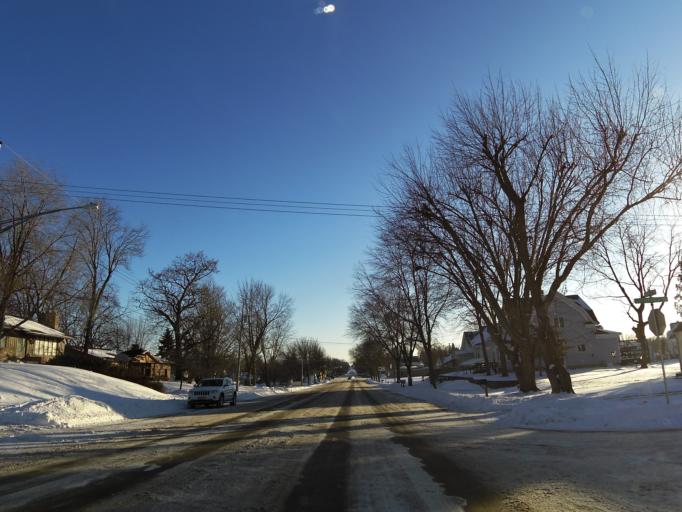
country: US
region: Minnesota
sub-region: Rice County
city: Lonsdale
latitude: 44.4837
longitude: -93.4286
